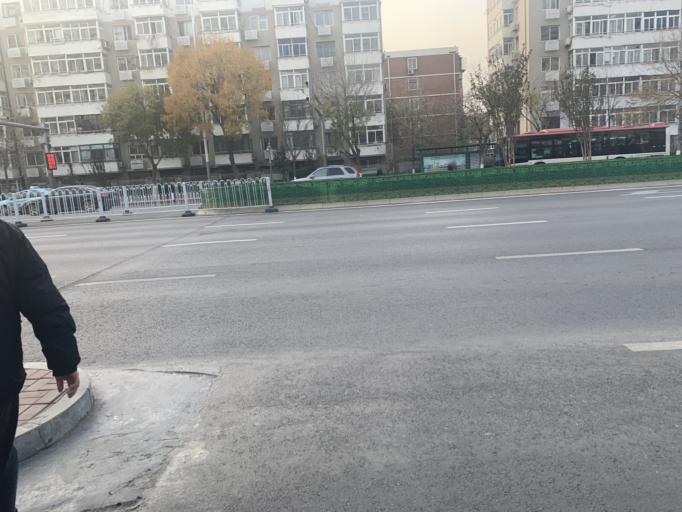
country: CN
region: Tianjin Shi
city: Wangdingdi
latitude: 39.0934
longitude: 117.1433
